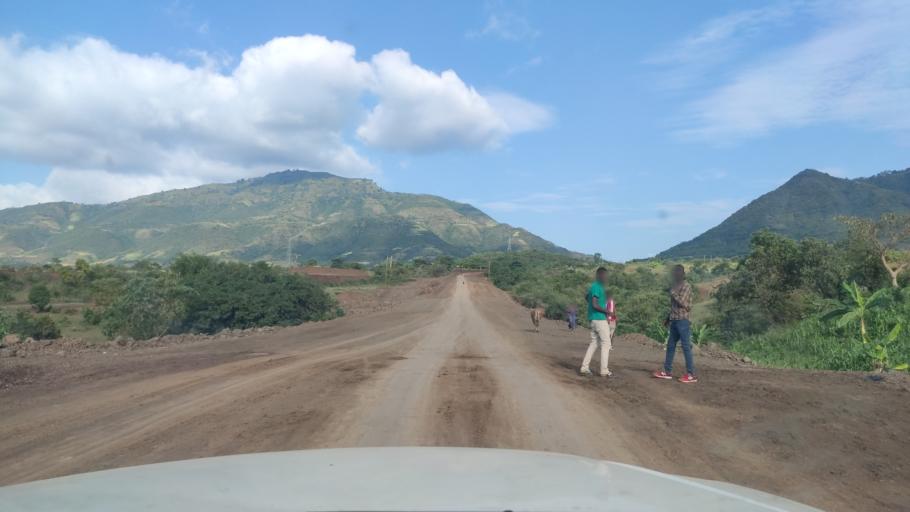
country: ET
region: Southern Nations, Nationalities, and People's Region
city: Arba Minch'
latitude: 6.4267
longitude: 37.3237
